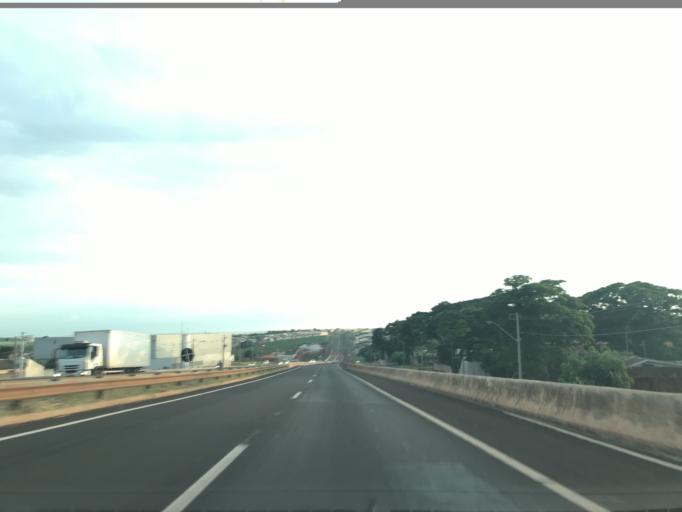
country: BR
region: Parana
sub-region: Maringa
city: Maringa
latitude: -23.3935
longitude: -51.9724
